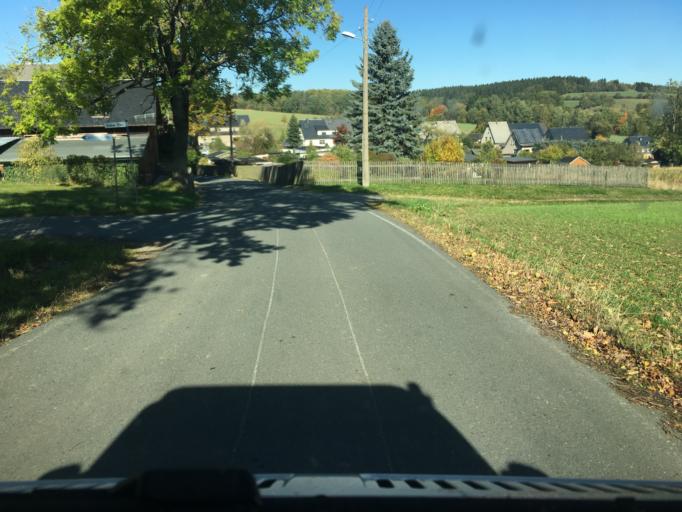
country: DE
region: Saxony
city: Schneeberg
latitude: 50.6031
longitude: 12.6174
